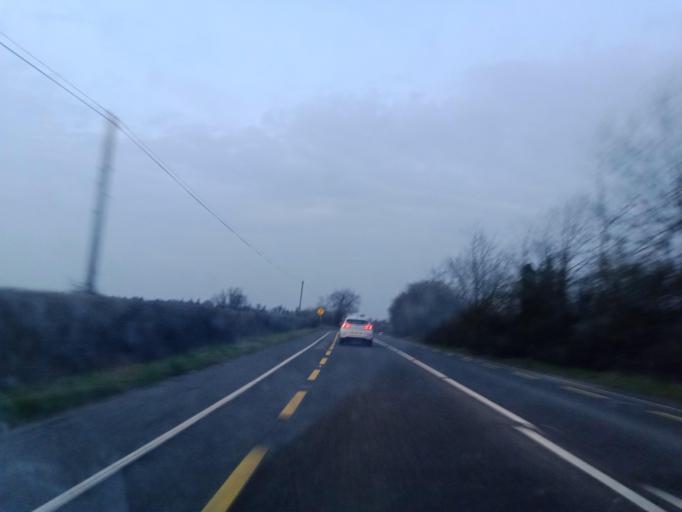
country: IE
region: Leinster
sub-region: Laois
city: Abbeyleix
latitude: 52.8708
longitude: -7.3637
